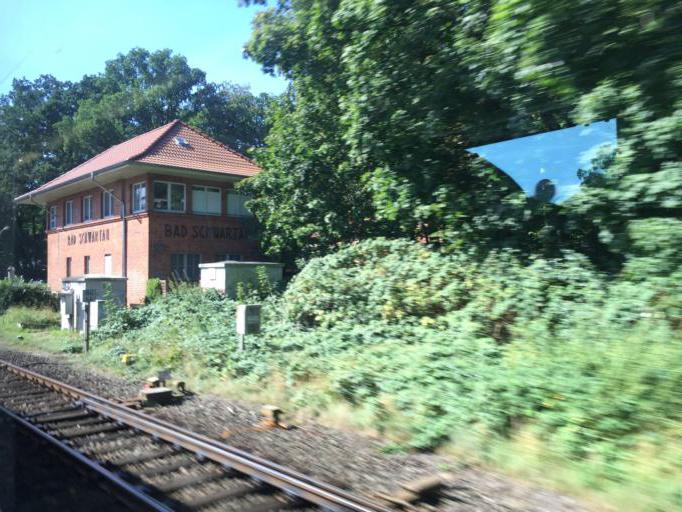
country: DE
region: Schleswig-Holstein
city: Bad Schwartau
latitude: 53.9198
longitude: 10.7068
